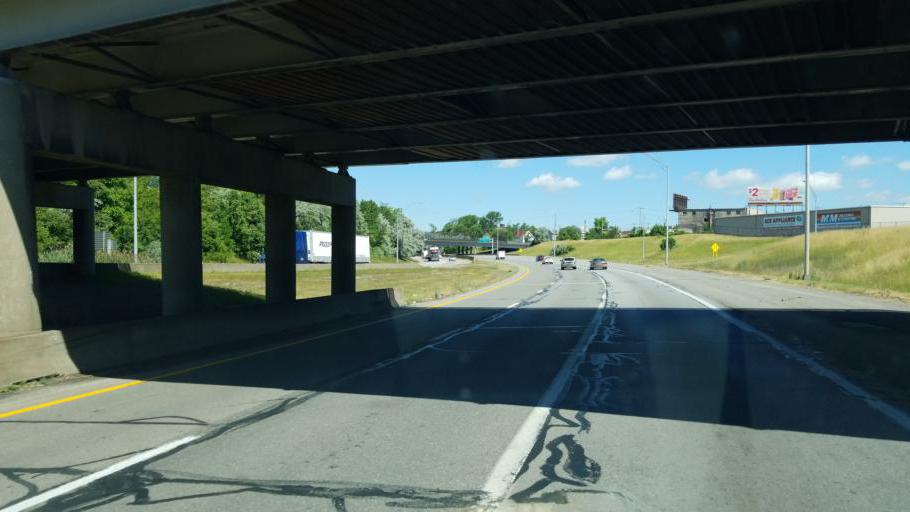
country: US
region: Ohio
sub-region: Lucas County
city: Toledo
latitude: 41.6502
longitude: -83.5487
